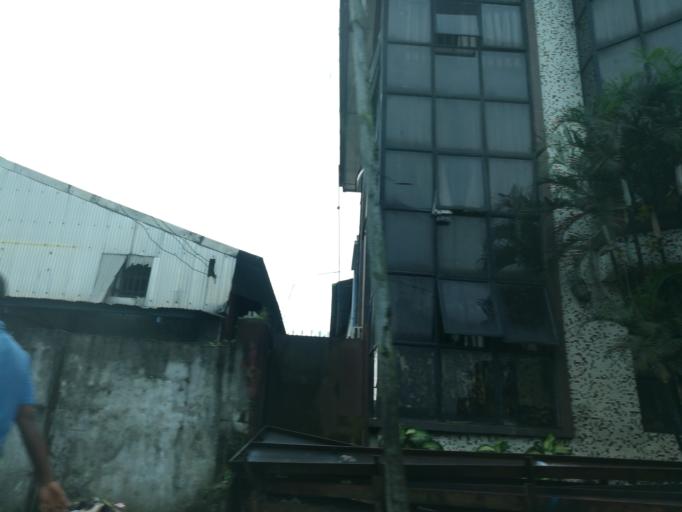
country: NG
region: Rivers
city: Port Harcourt
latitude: 4.7864
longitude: 7.0024
